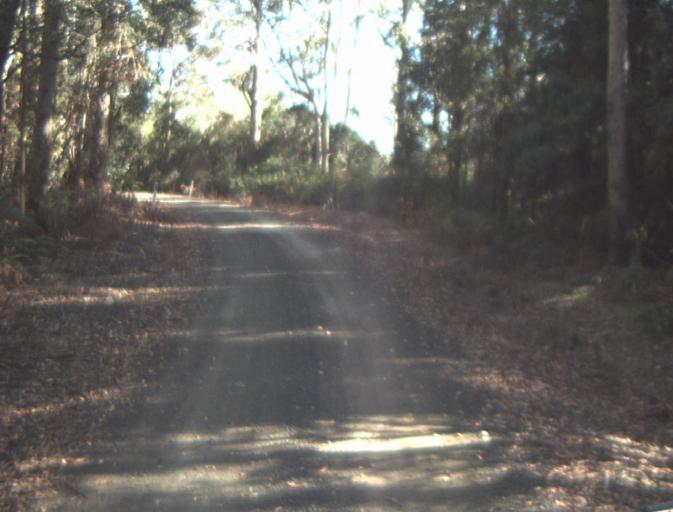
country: AU
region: Tasmania
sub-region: Dorset
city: Scottsdale
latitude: -41.2967
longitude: 147.3554
